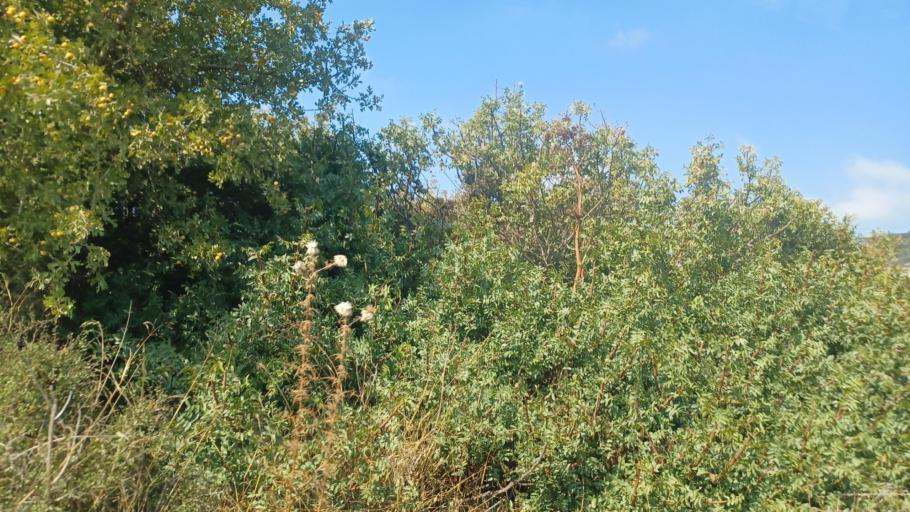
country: CY
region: Pafos
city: Mesogi
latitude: 34.8325
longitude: 32.4572
